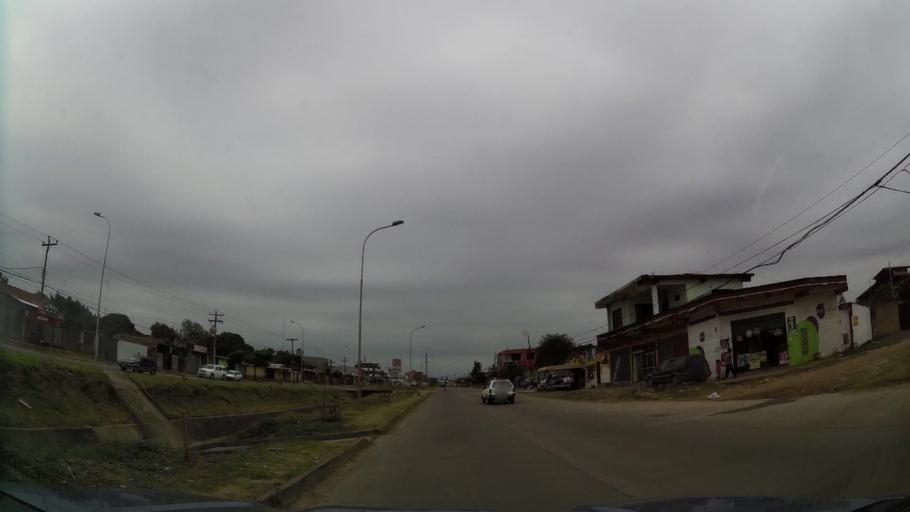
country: BO
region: Santa Cruz
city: Santa Cruz de la Sierra
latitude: -17.8323
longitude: -63.1824
